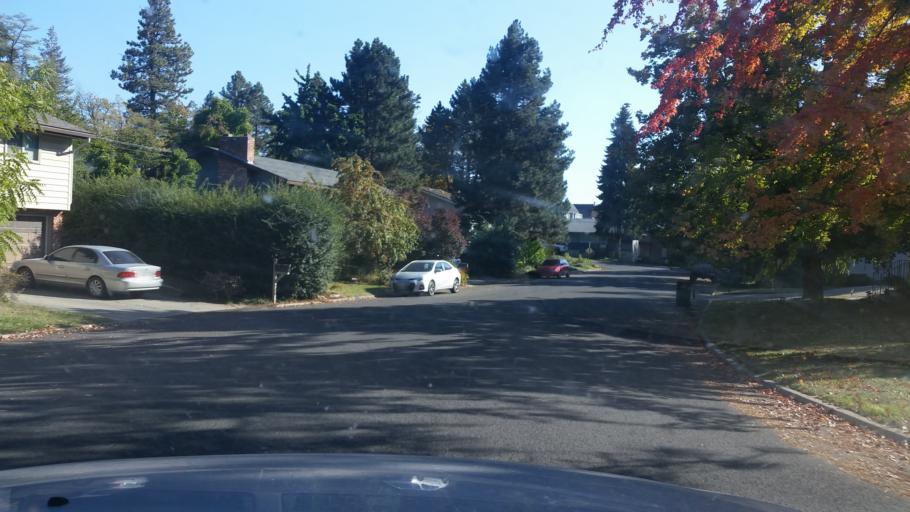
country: US
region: Washington
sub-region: Spokane County
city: Cheney
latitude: 47.4972
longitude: -117.5855
